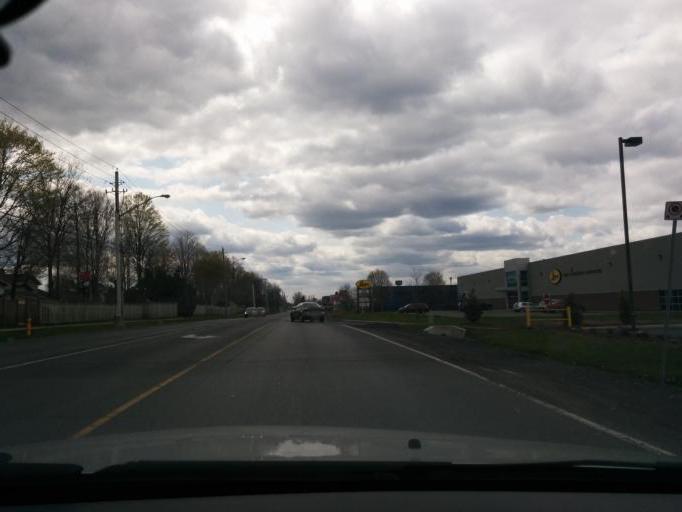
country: CA
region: Ontario
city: Cornwall
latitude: 45.0362
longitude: -74.7106
